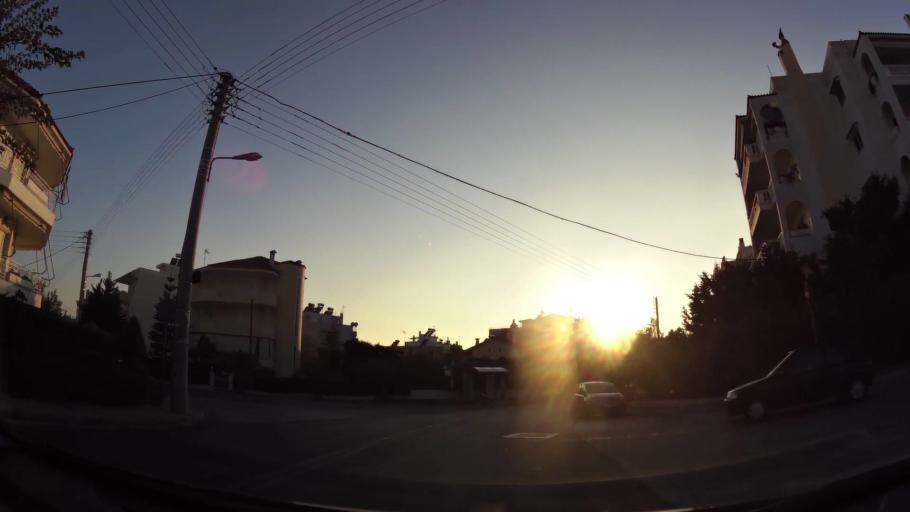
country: GR
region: Attica
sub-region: Nomarchia Athinas
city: Glyfada
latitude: 37.8799
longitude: 23.7665
